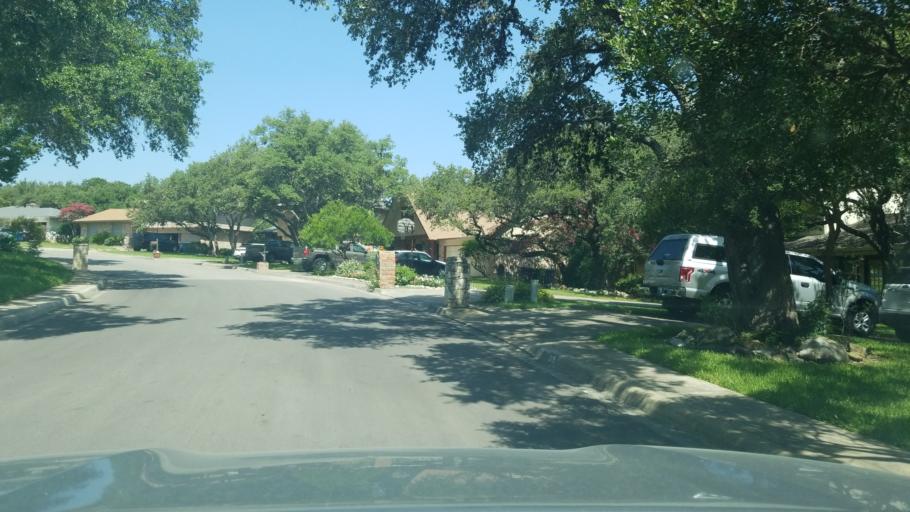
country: US
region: Texas
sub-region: Bexar County
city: Hollywood Park
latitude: 29.5888
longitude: -98.4612
